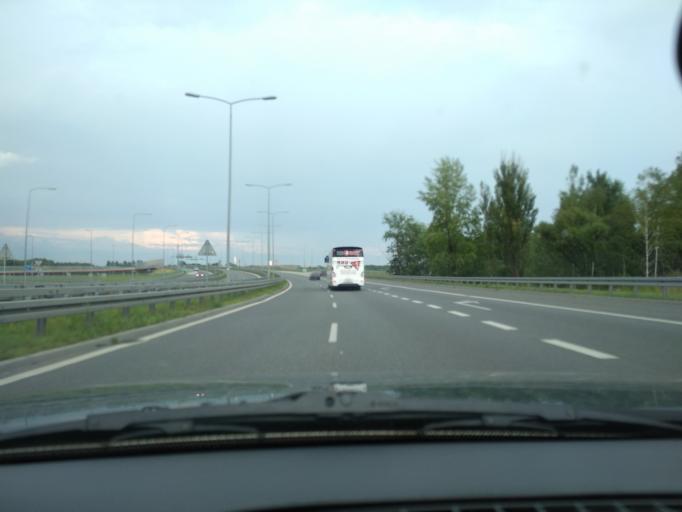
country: PL
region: Silesian Voivodeship
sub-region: Powiat gliwicki
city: Przyszowice
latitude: 50.2797
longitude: 18.7192
